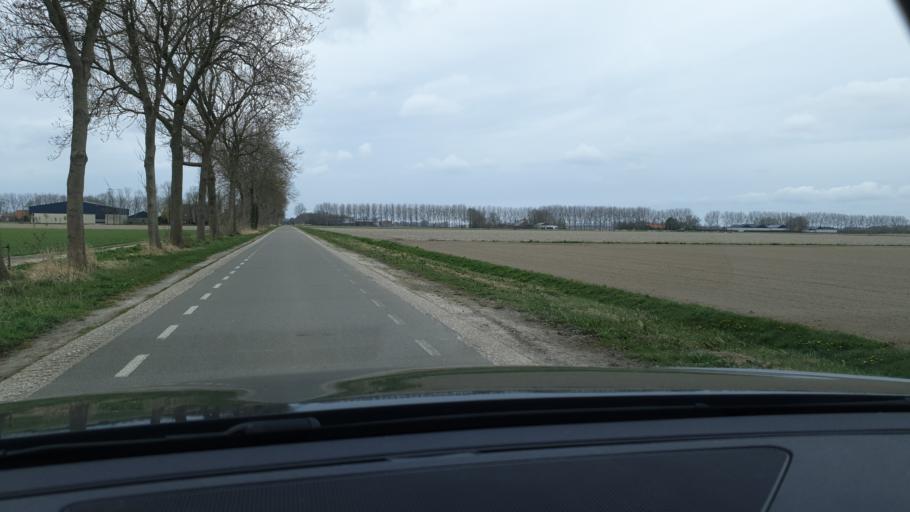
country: NL
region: Flevoland
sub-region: Gemeente Noordoostpolder
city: Emmeloord
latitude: 52.7090
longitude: 5.6941
